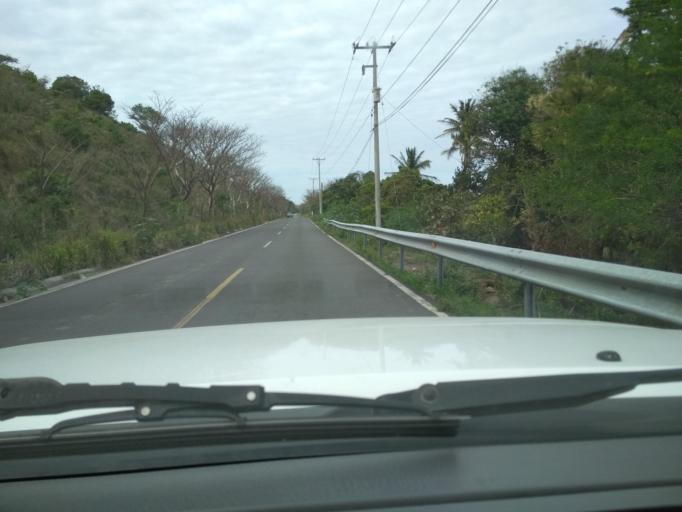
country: MX
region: Veracruz
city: Anton Lizardo
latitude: 19.0393
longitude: -95.9855
